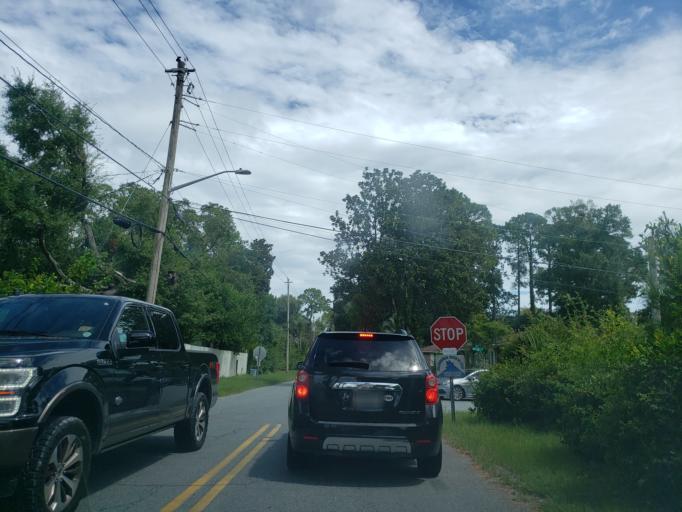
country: US
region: Georgia
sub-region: Chatham County
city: Thunderbolt
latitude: 32.0282
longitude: -81.0556
